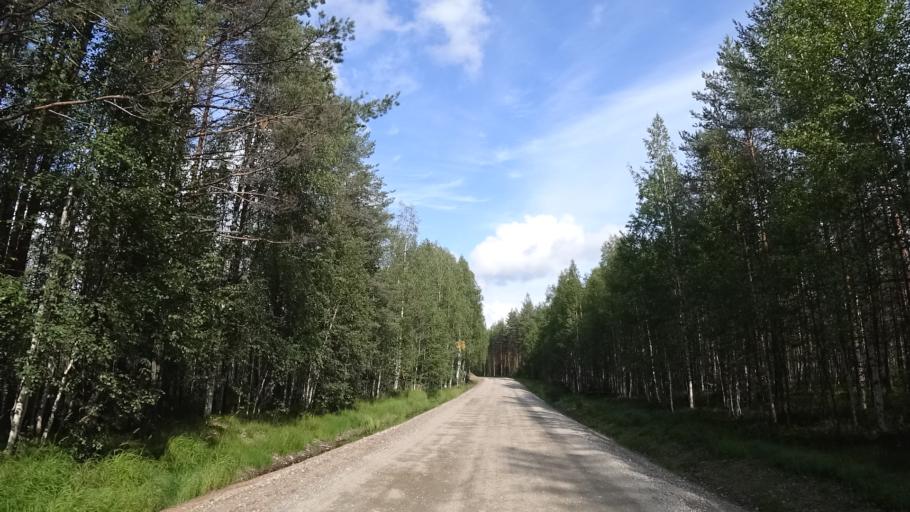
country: FI
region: North Karelia
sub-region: Pielisen Karjala
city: Lieksa
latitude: 63.5707
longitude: 30.1087
